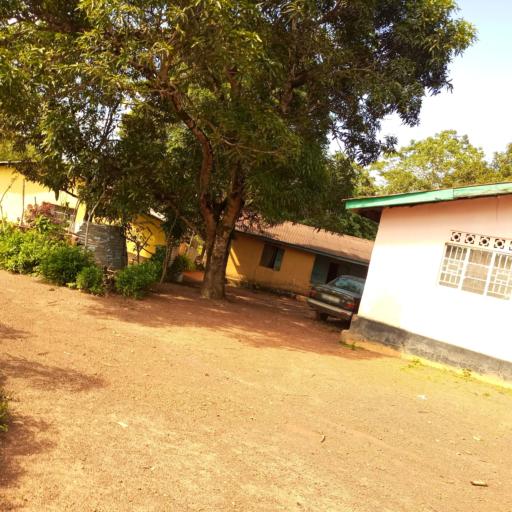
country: SL
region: Northern Province
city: Kambia
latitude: 9.1242
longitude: -12.9140
